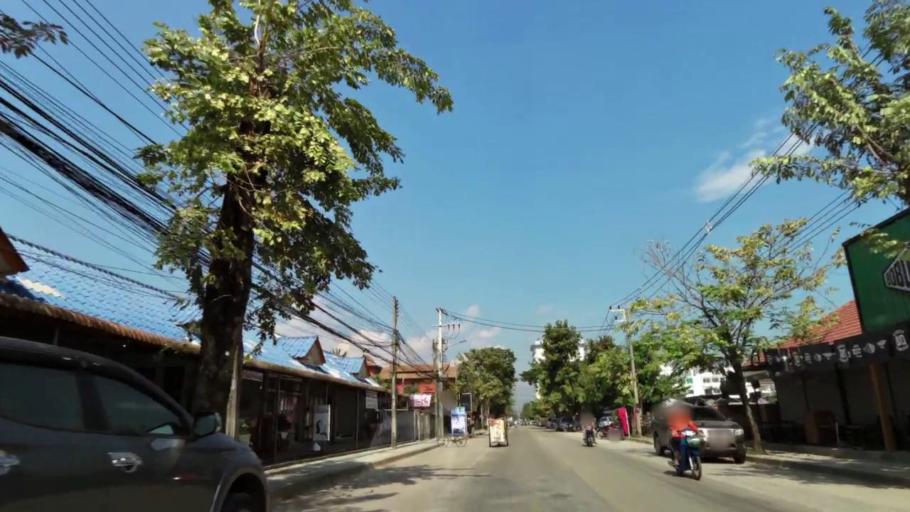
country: TH
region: Chiang Rai
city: Chiang Rai
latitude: 19.8968
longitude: 99.8277
